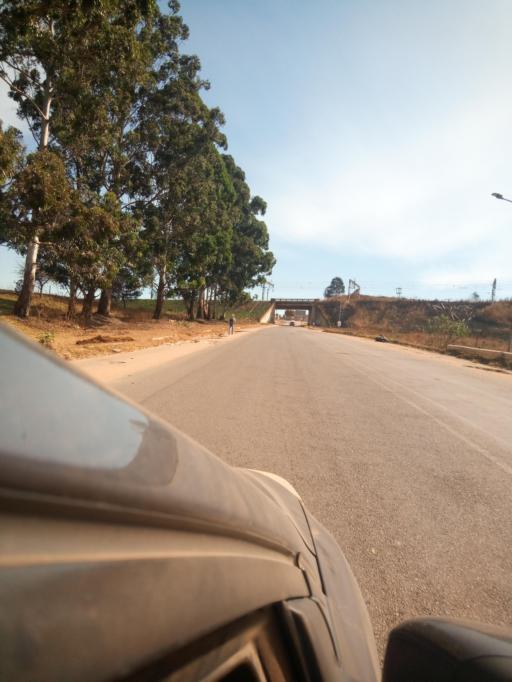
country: ZA
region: Mpumalanga
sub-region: Gert Sibande District Municipality
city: Piet Retief
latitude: -27.0184
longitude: 30.7930
